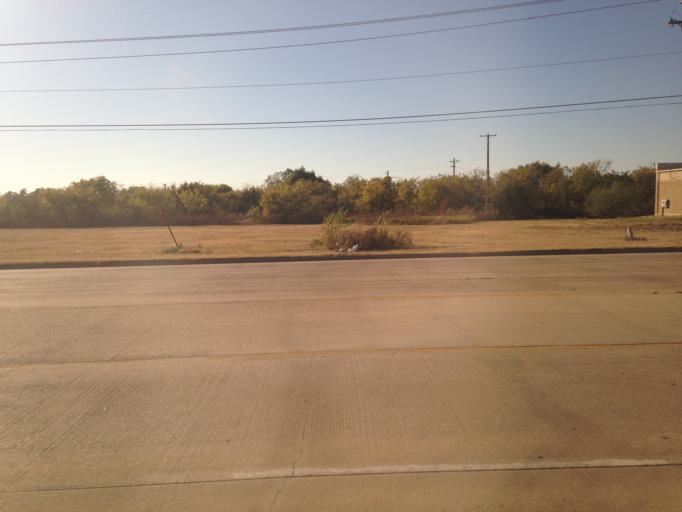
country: US
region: Texas
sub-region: Tarrant County
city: Watauga
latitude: 32.8567
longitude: -97.2639
